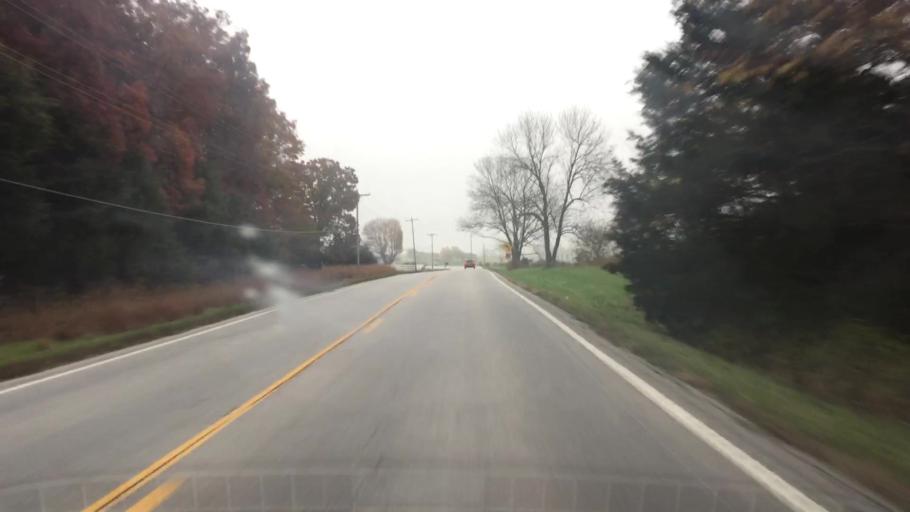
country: US
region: Missouri
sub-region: Callaway County
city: Fulton
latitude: 38.8749
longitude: -92.0692
